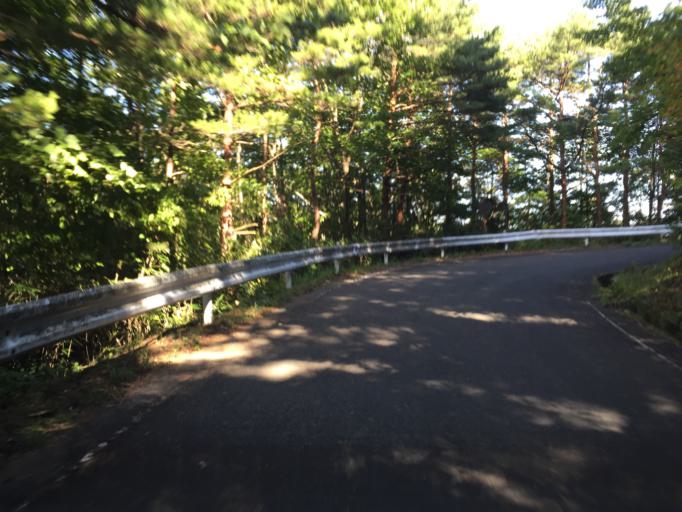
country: JP
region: Fukushima
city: Yanagawamachi-saiwaicho
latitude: 37.8449
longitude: 140.6934
